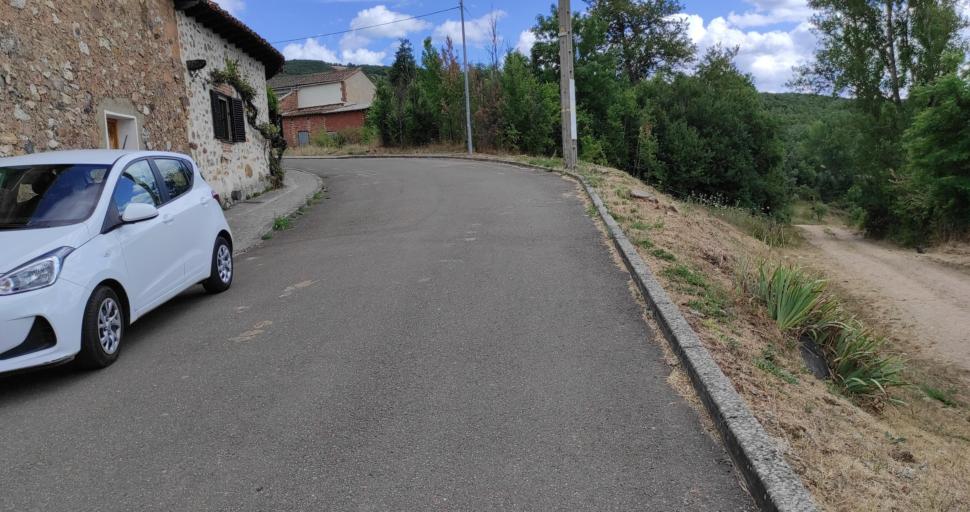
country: ES
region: Castille and Leon
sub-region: Provincia de Leon
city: Valdepielago
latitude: 42.8557
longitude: -5.3954
